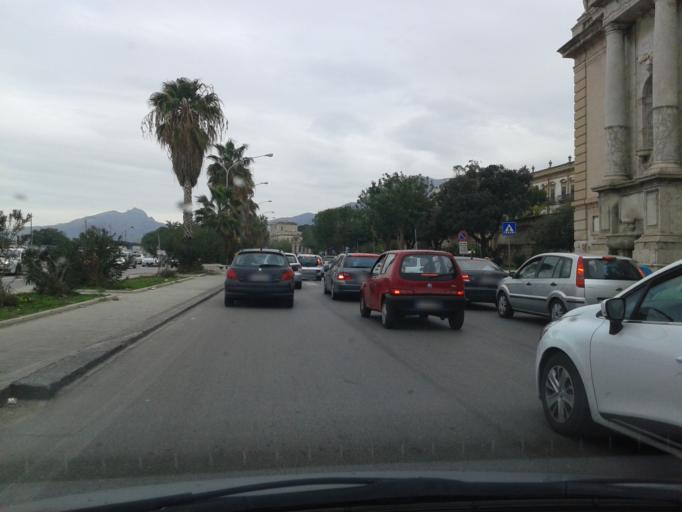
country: IT
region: Sicily
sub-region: Palermo
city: Palermo
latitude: 38.1199
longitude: 13.3714
